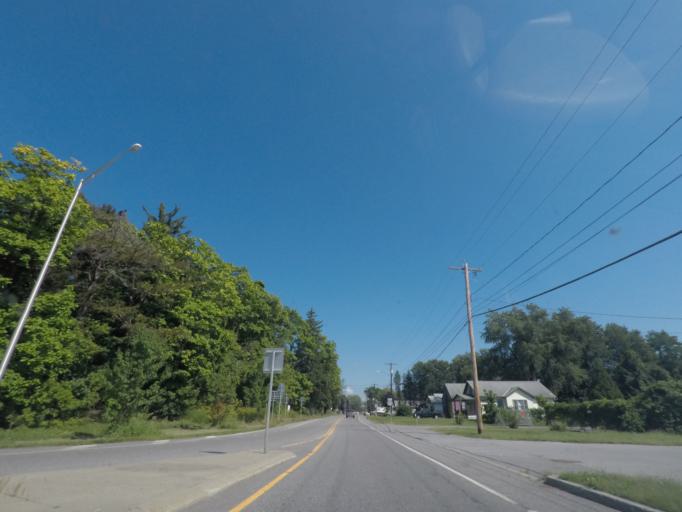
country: US
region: New York
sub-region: Albany County
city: Roessleville
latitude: 42.7388
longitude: -73.7904
